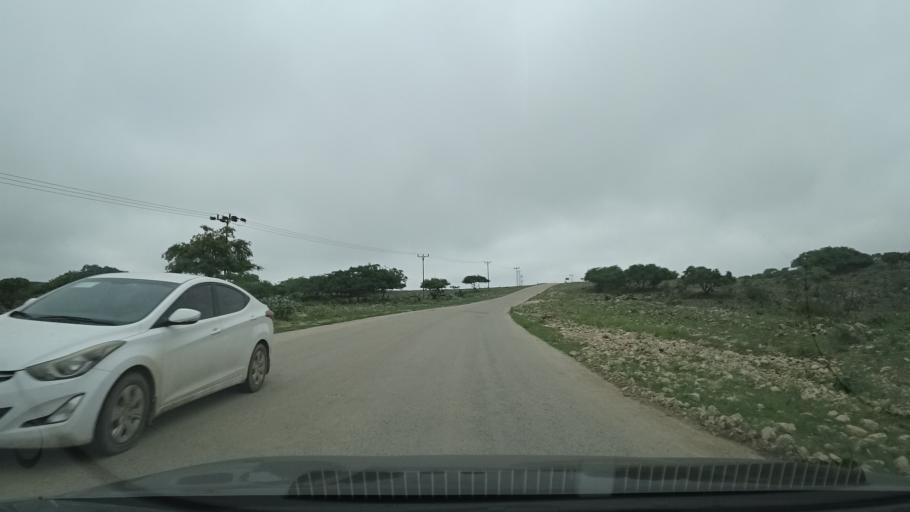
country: OM
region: Zufar
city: Salalah
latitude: 17.1194
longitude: 54.5771
